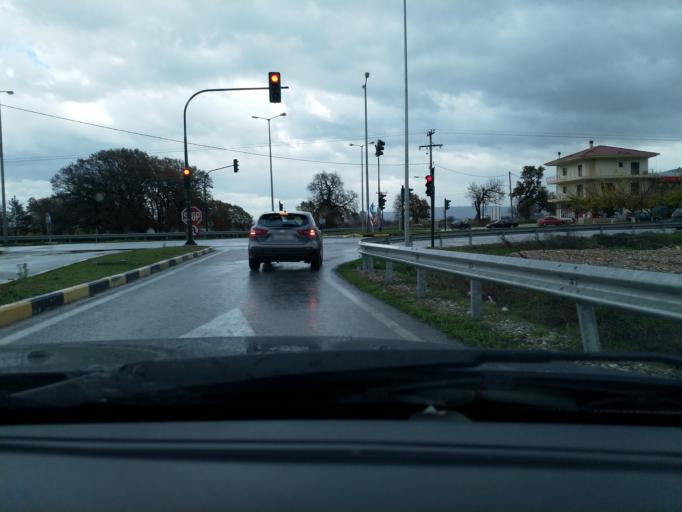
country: GR
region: Thessaly
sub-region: Trikala
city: Gomfoi
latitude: 39.4857
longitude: 21.6753
